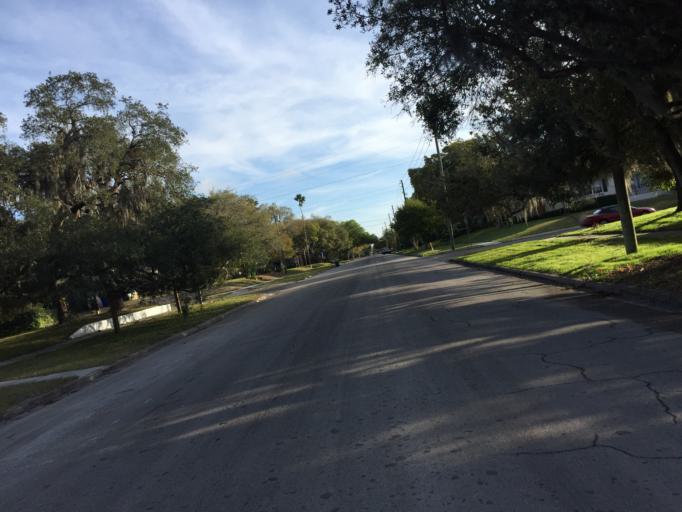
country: US
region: Florida
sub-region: Pinellas County
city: Clearwater
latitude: 27.9722
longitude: -82.7744
